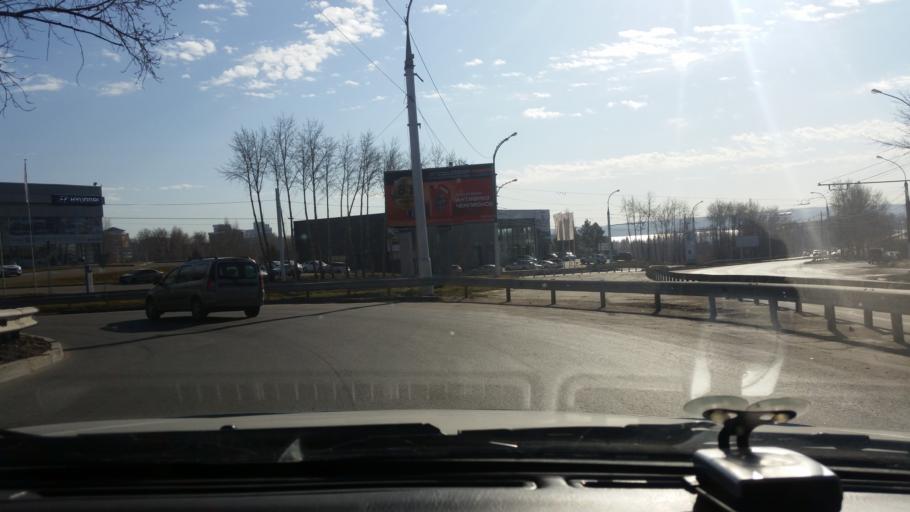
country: RU
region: Irkutsk
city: Dzerzhinsk
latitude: 52.2606
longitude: 104.3506
